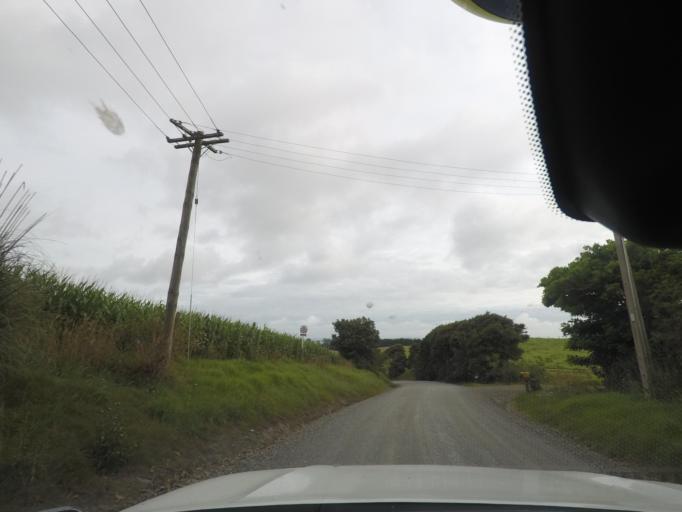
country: NZ
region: Auckland
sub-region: Auckland
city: Parakai
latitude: -36.4745
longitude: 174.2573
